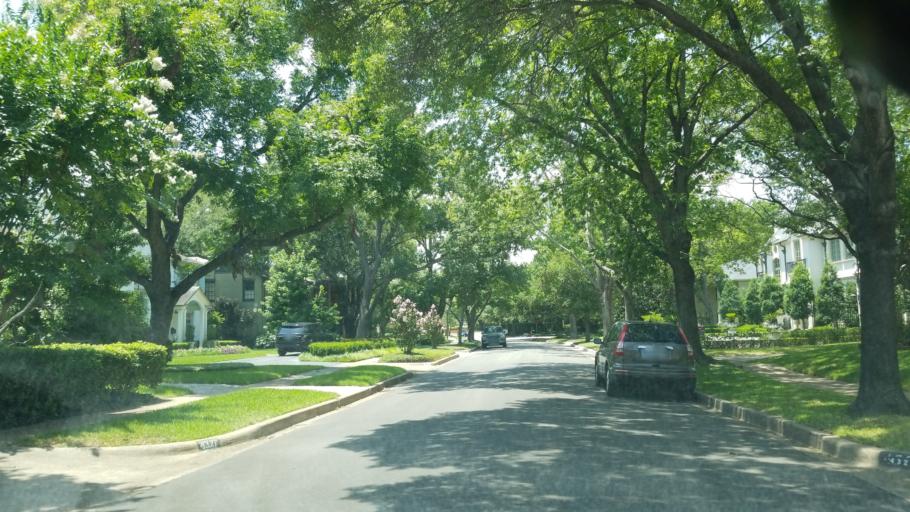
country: US
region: Texas
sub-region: Dallas County
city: Highland Park
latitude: 32.8312
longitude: -96.8087
